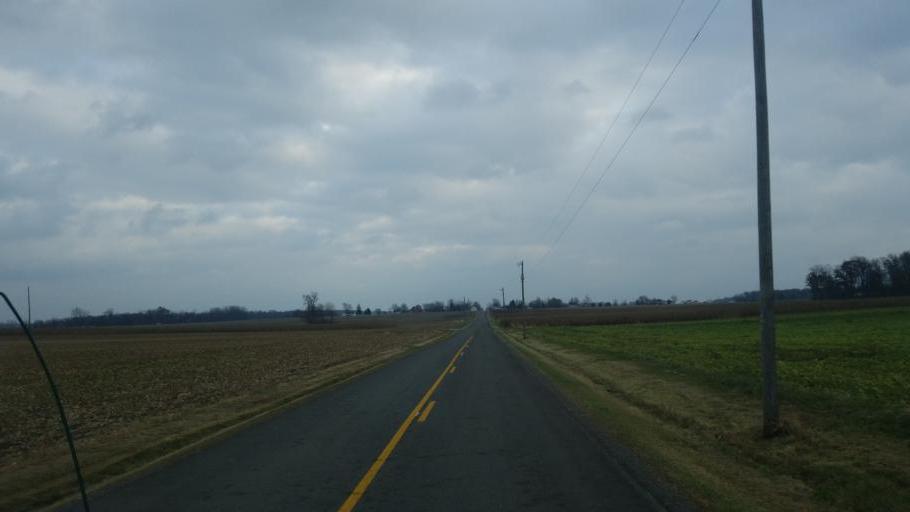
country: US
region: Ohio
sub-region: Mercer County
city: Coldwater
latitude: 40.5090
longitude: -84.7194
